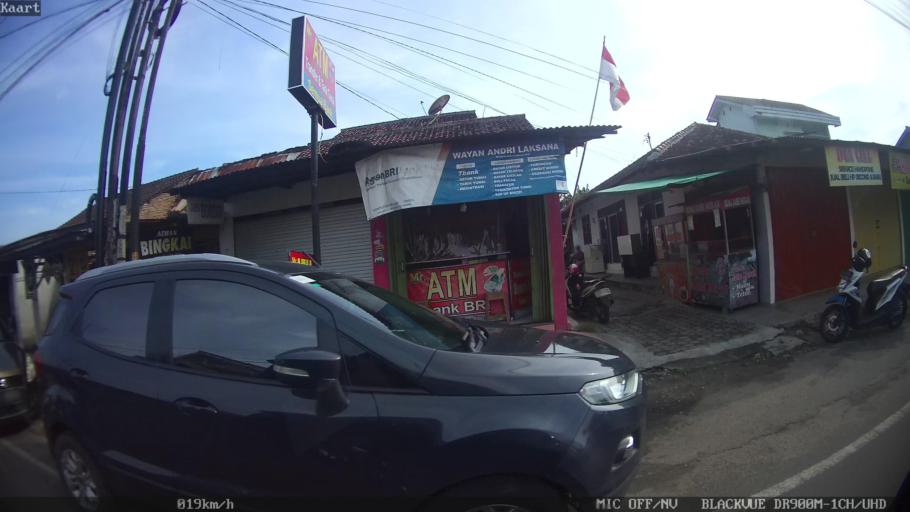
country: ID
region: Lampung
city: Kedaton
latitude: -5.3858
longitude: 105.2687
